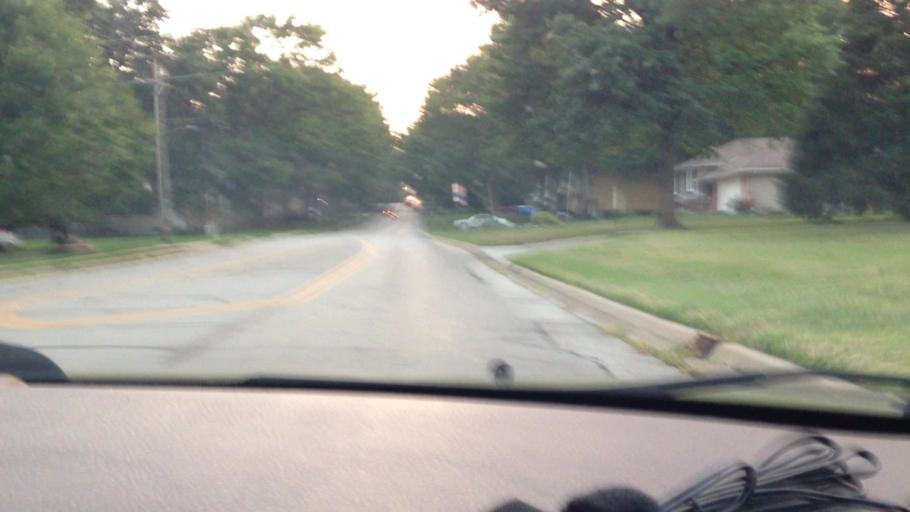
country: US
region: Kansas
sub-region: Leavenworth County
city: Leavenworth
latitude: 39.2886
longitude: -94.9291
